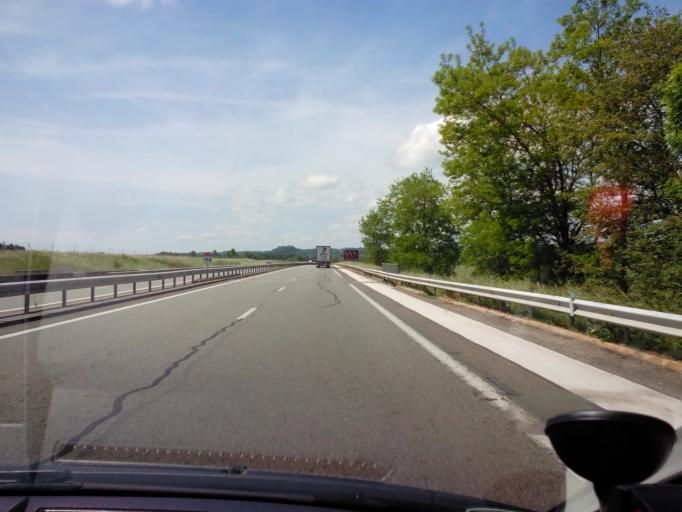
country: FR
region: Champagne-Ardenne
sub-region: Departement de la Haute-Marne
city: Avrecourt
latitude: 48.0245
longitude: 5.5385
